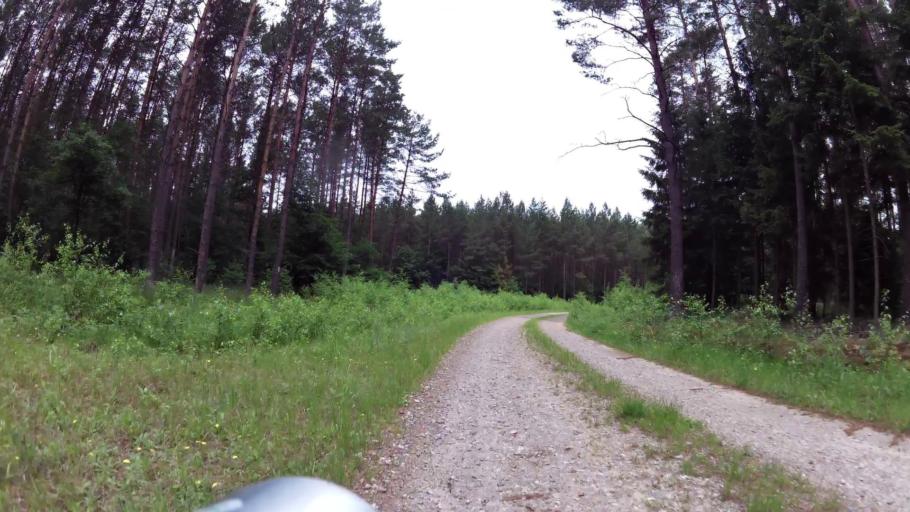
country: PL
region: West Pomeranian Voivodeship
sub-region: Powiat szczecinecki
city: Bialy Bor
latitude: 53.9177
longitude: 16.8302
